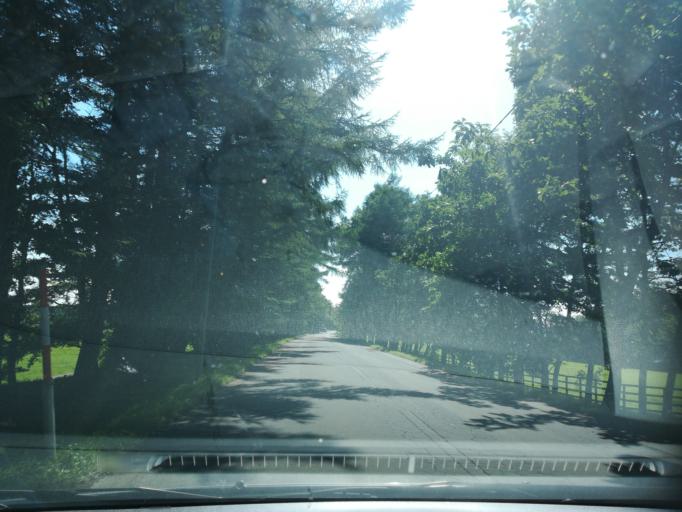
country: JP
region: Hokkaido
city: Chitose
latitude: 42.9187
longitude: 141.8632
